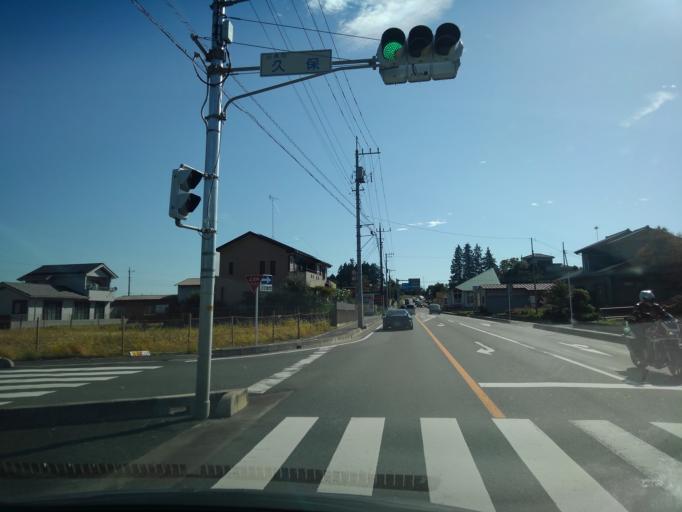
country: JP
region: Saitama
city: Hanno
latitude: 35.8839
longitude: 139.3011
